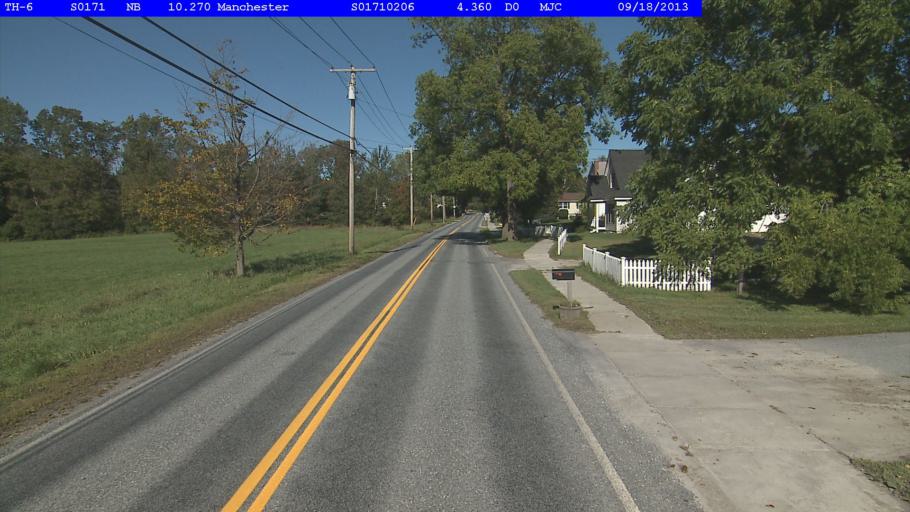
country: US
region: Vermont
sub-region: Bennington County
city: Manchester Center
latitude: 43.1661
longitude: -73.0511
